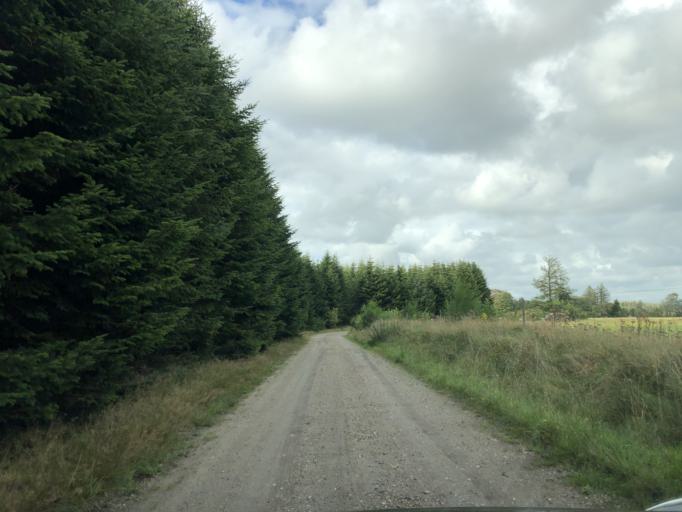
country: DK
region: Central Jutland
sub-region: Holstebro Kommune
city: Ulfborg
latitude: 56.2475
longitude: 8.3861
